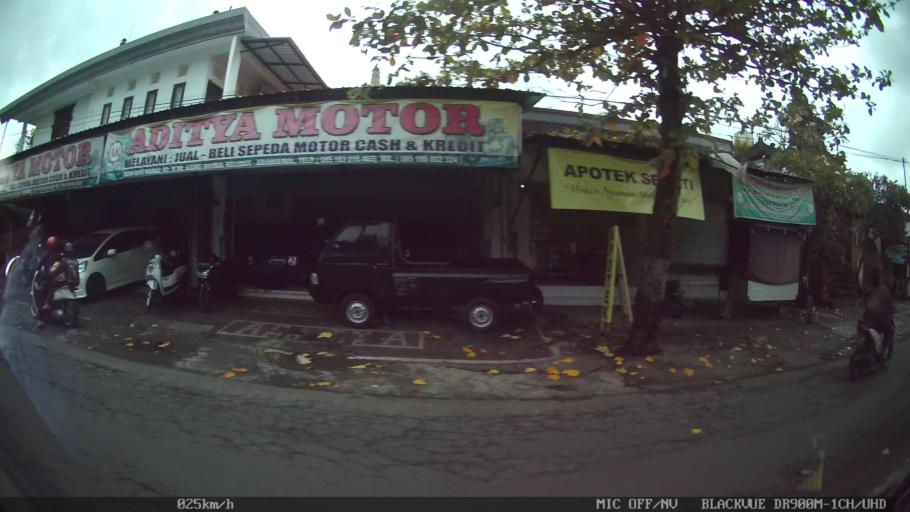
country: ID
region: Bali
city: Banjar Mambalkajanan
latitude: -8.5517
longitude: 115.2196
